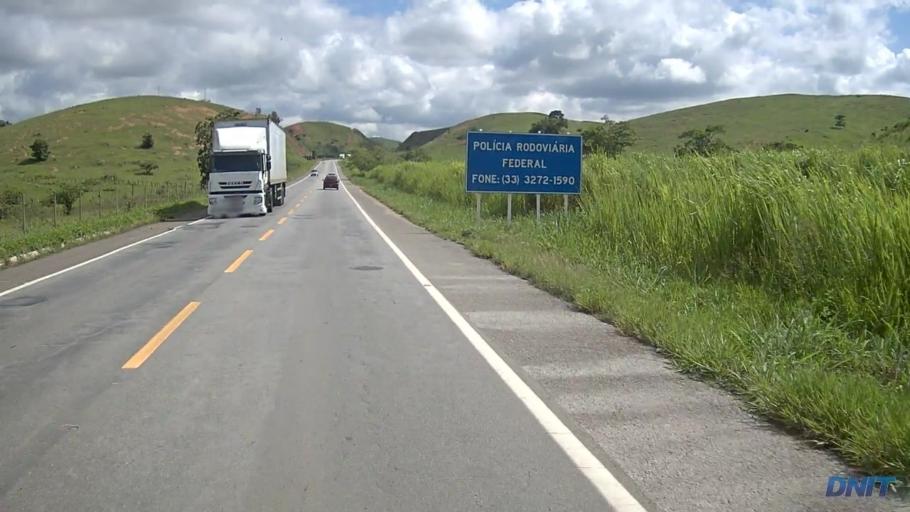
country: BR
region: Minas Gerais
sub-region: Belo Oriente
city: Belo Oriente
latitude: -19.1304
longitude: -42.2134
